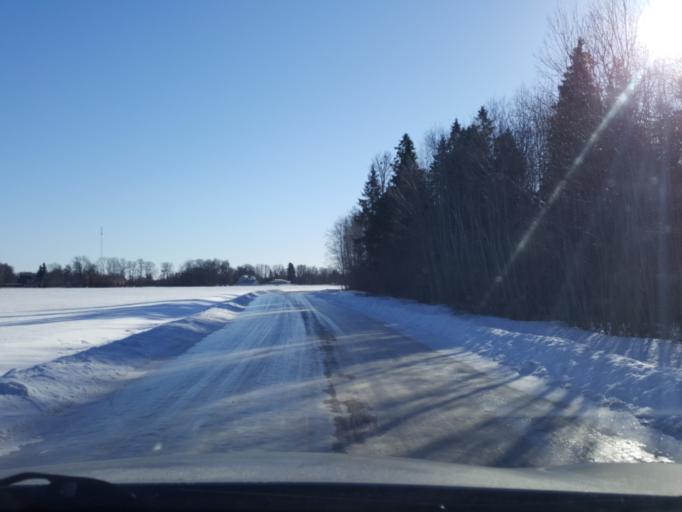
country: EE
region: Viljandimaa
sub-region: Viljandi linn
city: Viljandi
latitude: 58.4647
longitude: 25.5777
